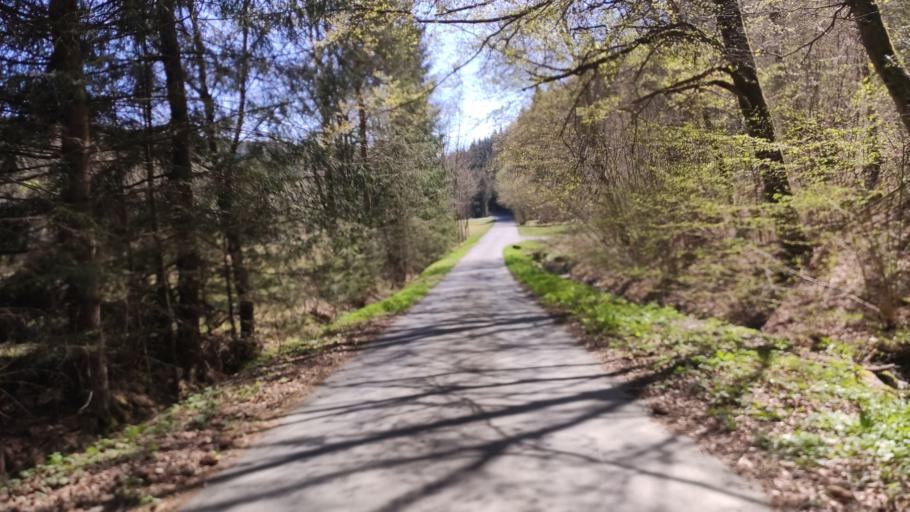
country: DE
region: Bavaria
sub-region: Upper Franconia
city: Nordhalben
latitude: 50.3613
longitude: 11.4824
